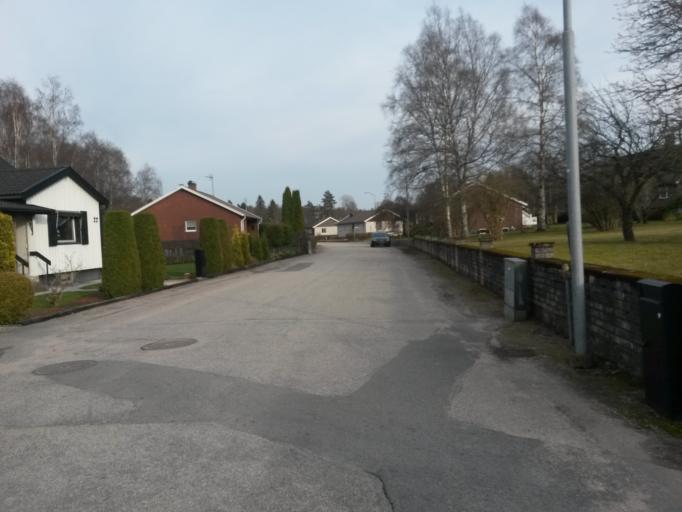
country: SE
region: Vaestra Goetaland
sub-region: Herrljunga Kommun
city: Herrljunga
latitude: 58.0715
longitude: 13.0248
